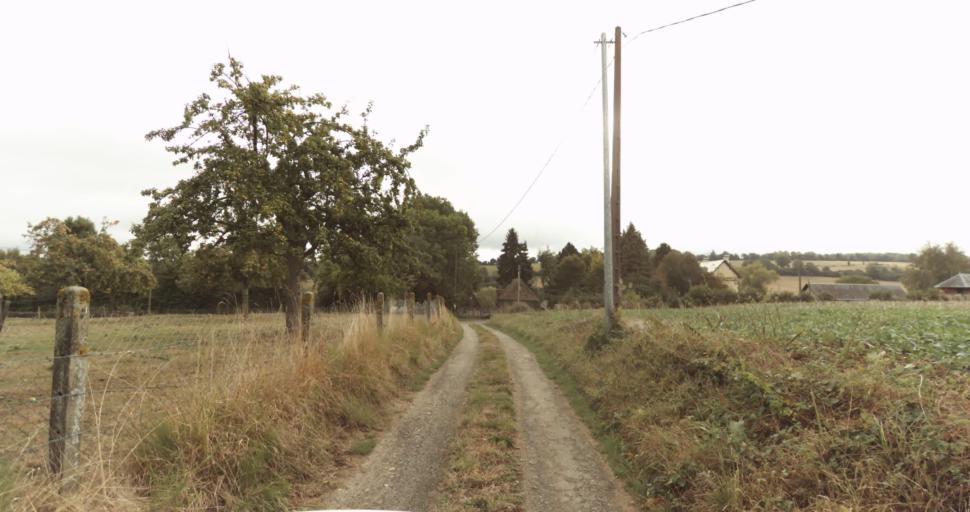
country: FR
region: Lower Normandy
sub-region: Departement du Calvados
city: Livarot
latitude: 48.9299
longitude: 0.1082
